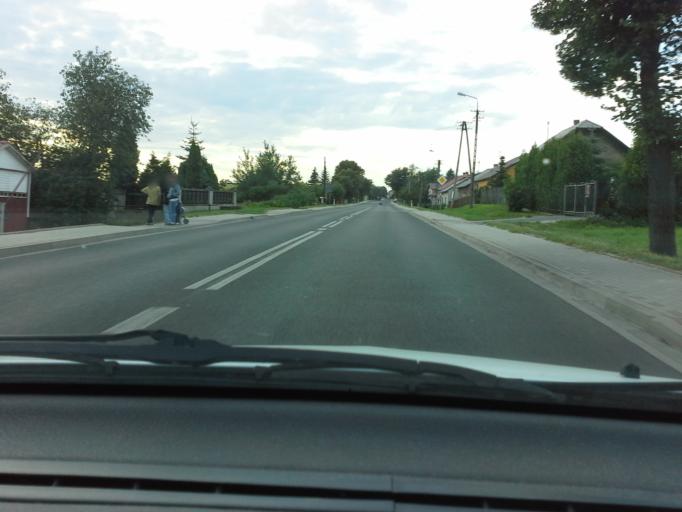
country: PL
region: Lesser Poland Voivodeship
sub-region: Powiat chrzanowski
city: Trzebinia
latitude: 50.1532
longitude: 19.4856
